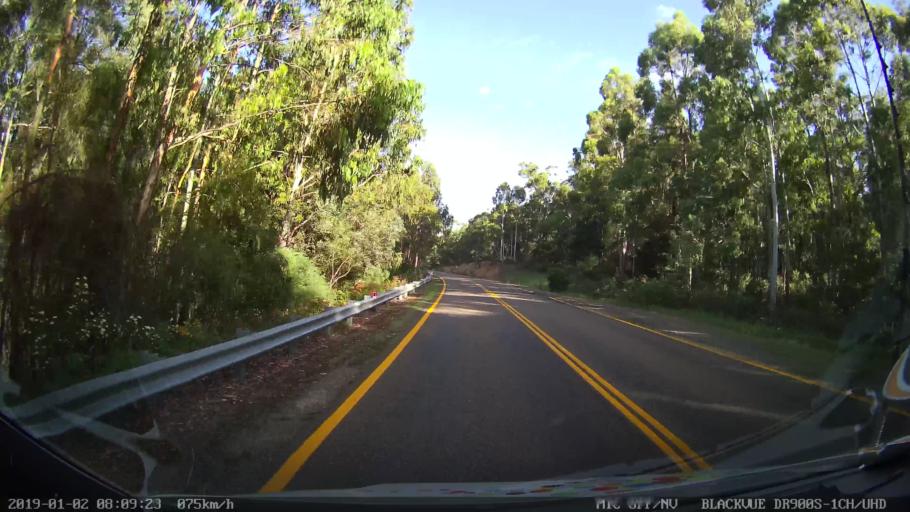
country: AU
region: New South Wales
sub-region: Tumut Shire
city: Tumut
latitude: -35.6073
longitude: 148.3801
